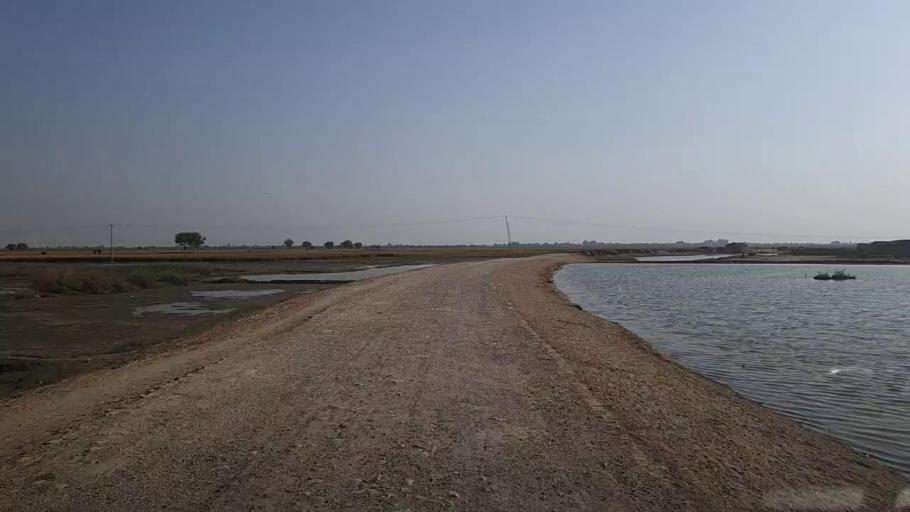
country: PK
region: Sindh
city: Kandhkot
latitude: 28.3708
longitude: 69.3330
